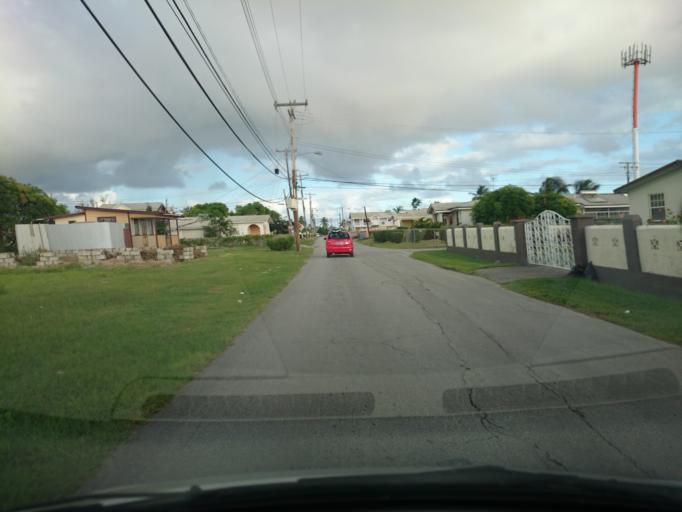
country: BB
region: Christ Church
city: Oistins
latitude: 13.0534
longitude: -59.5138
